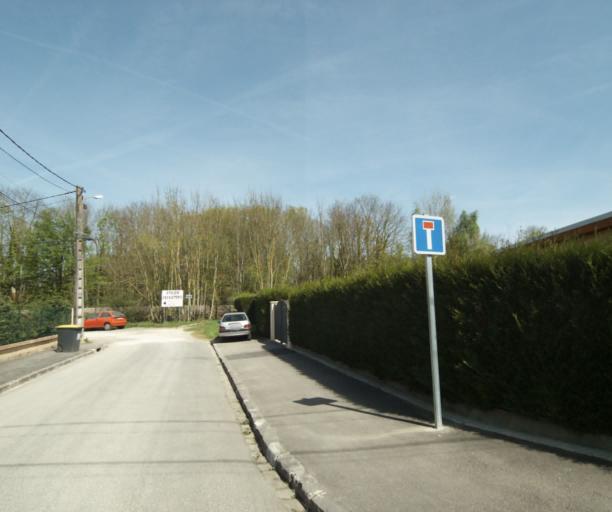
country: FR
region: Ile-de-France
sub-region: Departement de Seine-et-Marne
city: Nangis
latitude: 48.5586
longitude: 3.0190
